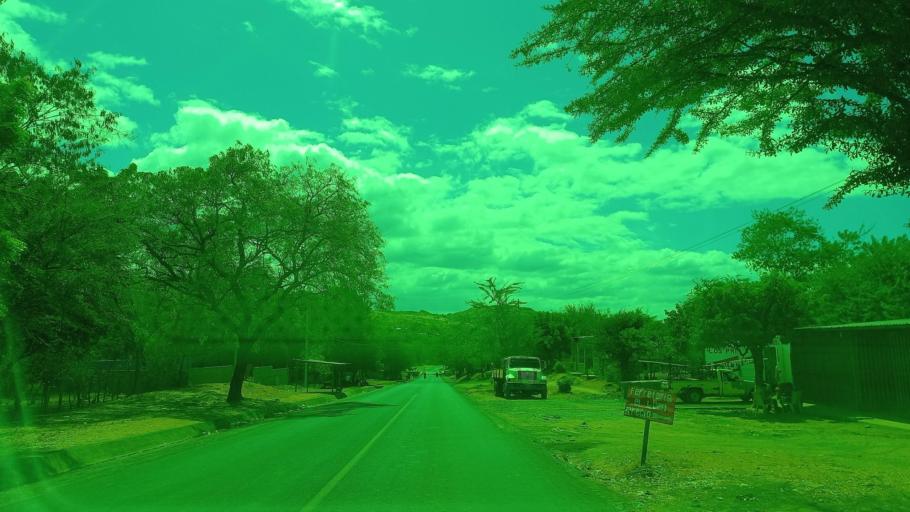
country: NI
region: Managua
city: Ciudad Sandino
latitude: 12.1898
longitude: -86.3366
